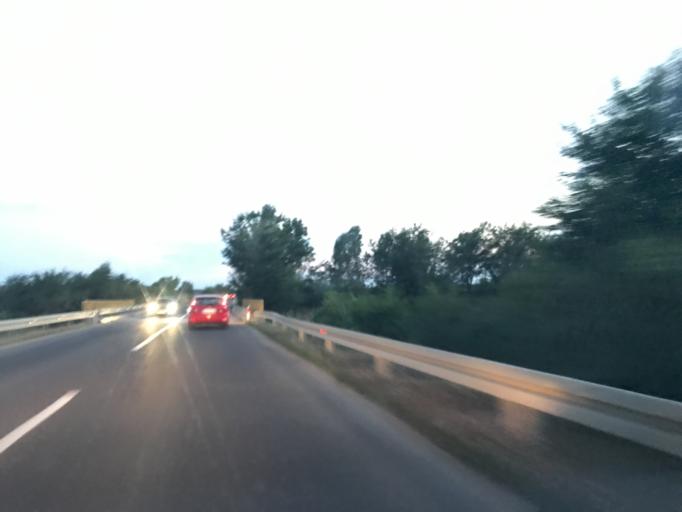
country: RS
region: Central Serbia
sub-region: Branicevski Okrug
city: Pozarevac
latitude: 44.6140
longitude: 21.1447
